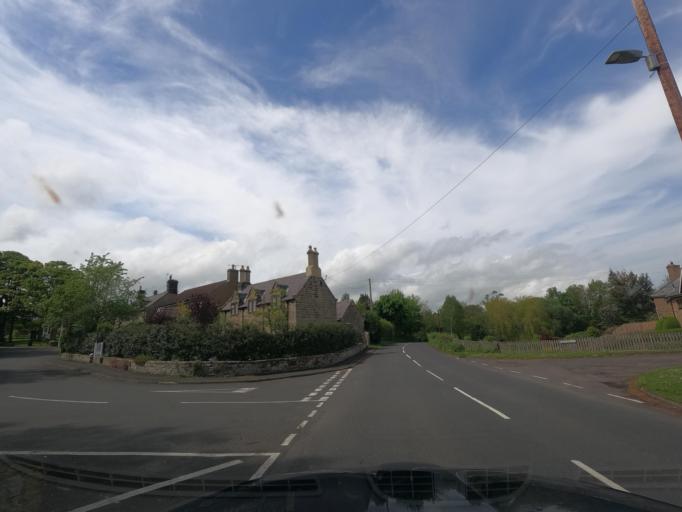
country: GB
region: England
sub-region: Northumberland
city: Whittingham
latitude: 55.4009
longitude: -1.8900
